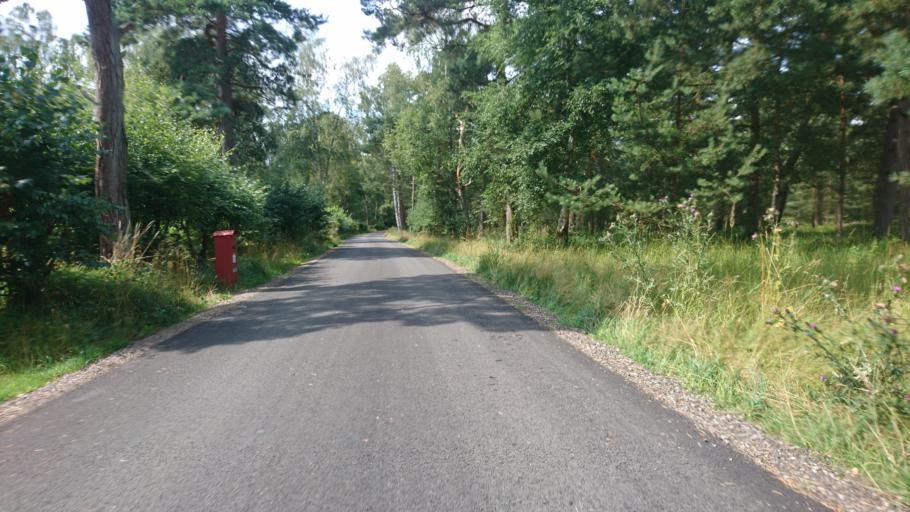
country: SE
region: Skane
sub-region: Vellinge Kommun
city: Ljunghusen
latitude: 55.3942
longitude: 12.9283
